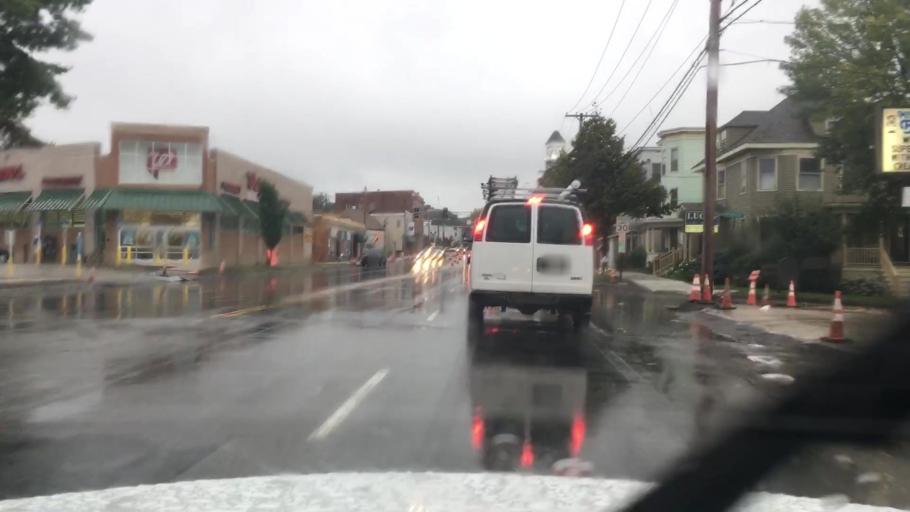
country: US
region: Maine
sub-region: Cumberland County
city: Portland
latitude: 43.6695
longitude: -70.2822
